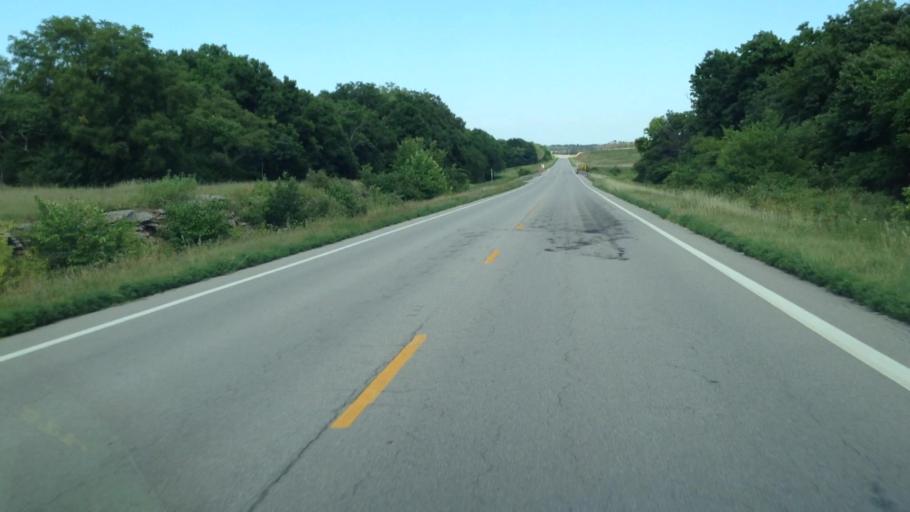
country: US
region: Kansas
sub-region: Neosho County
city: Erie
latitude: 37.6888
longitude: -95.1834
